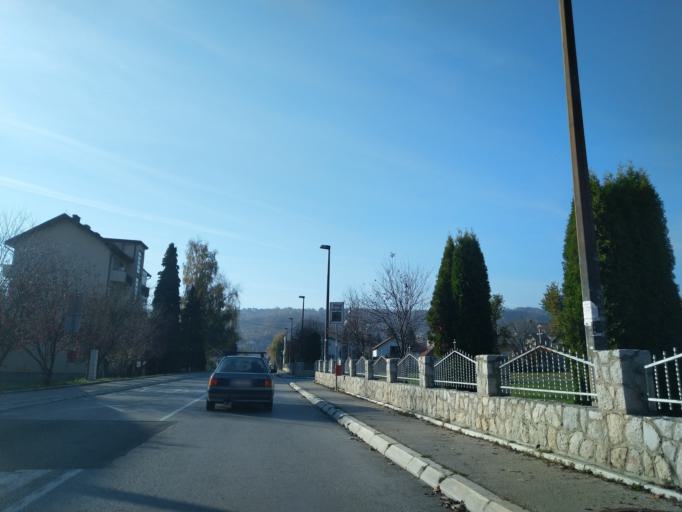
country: RS
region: Central Serbia
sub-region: Zlatiborski Okrug
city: Uzice
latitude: 43.8452
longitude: 19.8960
